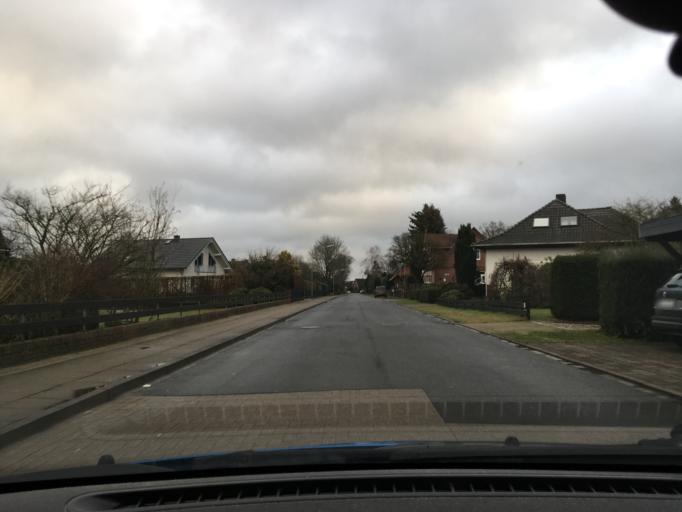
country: DE
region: Lower Saxony
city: Winsen
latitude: 53.3325
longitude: 10.2005
